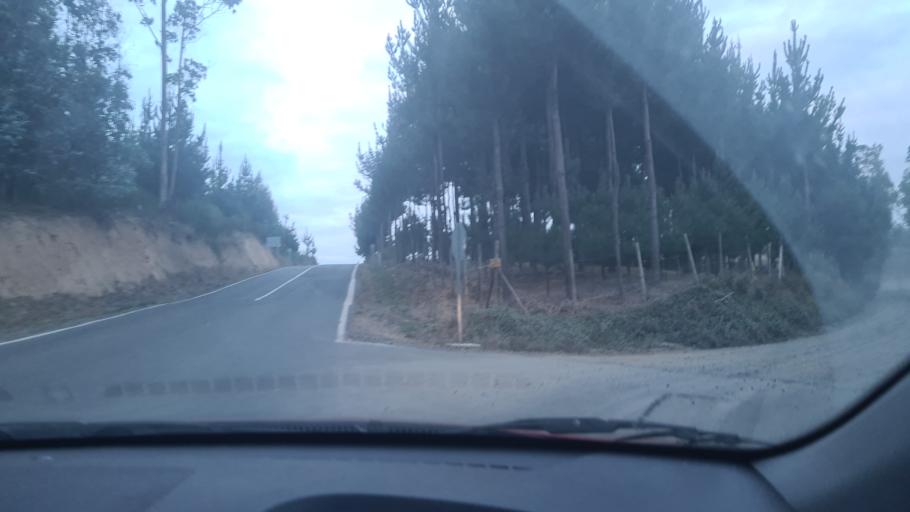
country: CL
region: Biobio
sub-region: Provincia de Concepcion
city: Tome
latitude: -36.6539
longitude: -72.7832
